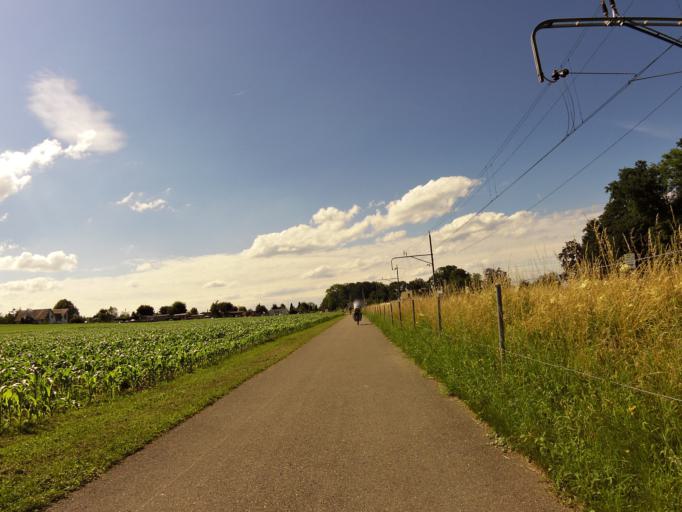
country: CH
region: Thurgau
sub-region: Arbon District
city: Egnach
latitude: 47.5355
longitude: 9.4028
